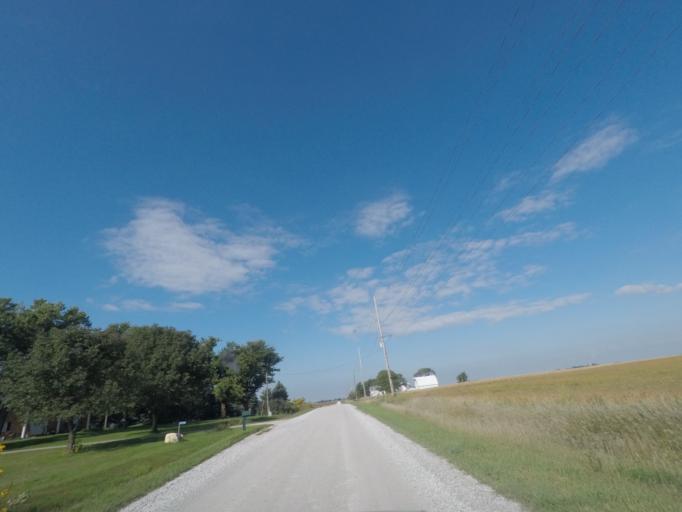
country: US
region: Iowa
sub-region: Story County
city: Nevada
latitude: 42.0345
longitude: -93.4100
